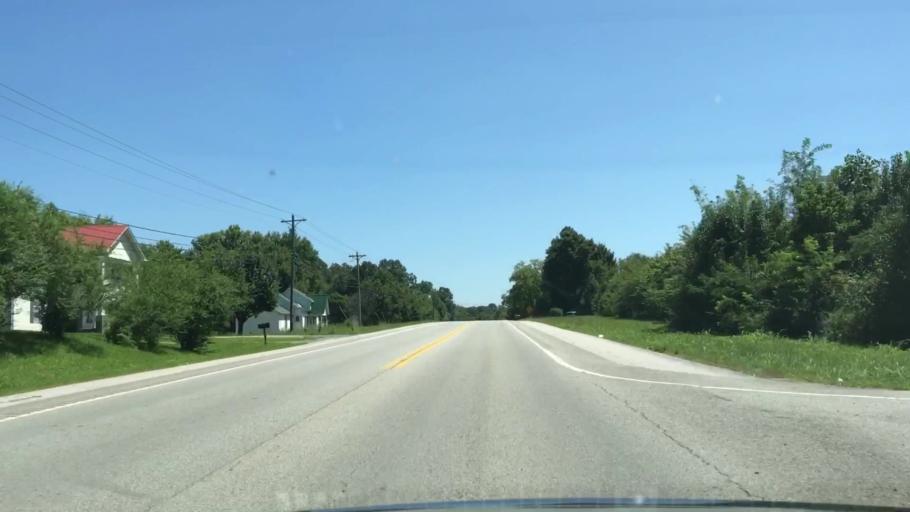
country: US
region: Tennessee
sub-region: Jackson County
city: Gainesboro
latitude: 36.2925
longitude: -85.6374
